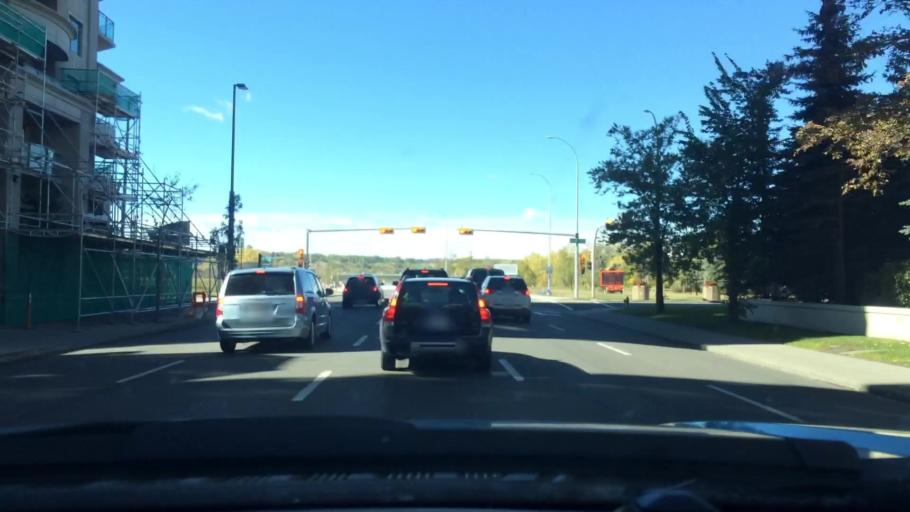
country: CA
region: Alberta
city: Calgary
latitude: 51.0481
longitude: -114.0877
